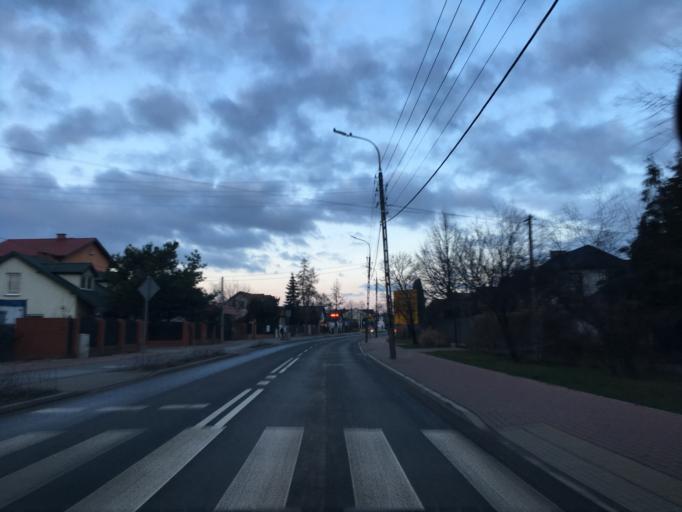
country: PL
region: Masovian Voivodeship
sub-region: Powiat grodziski
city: Grodzisk Mazowiecki
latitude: 52.1022
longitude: 20.6388
